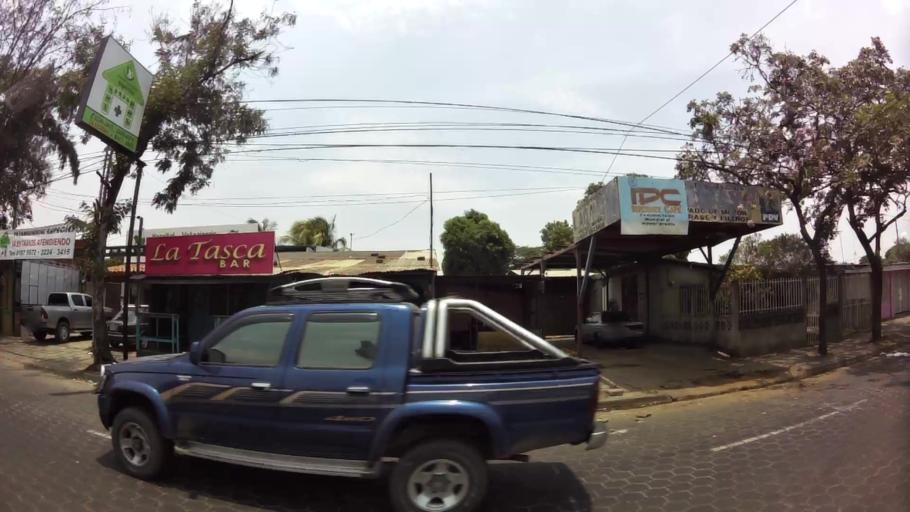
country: NI
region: Managua
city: Managua
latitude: 12.1380
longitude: -86.2910
